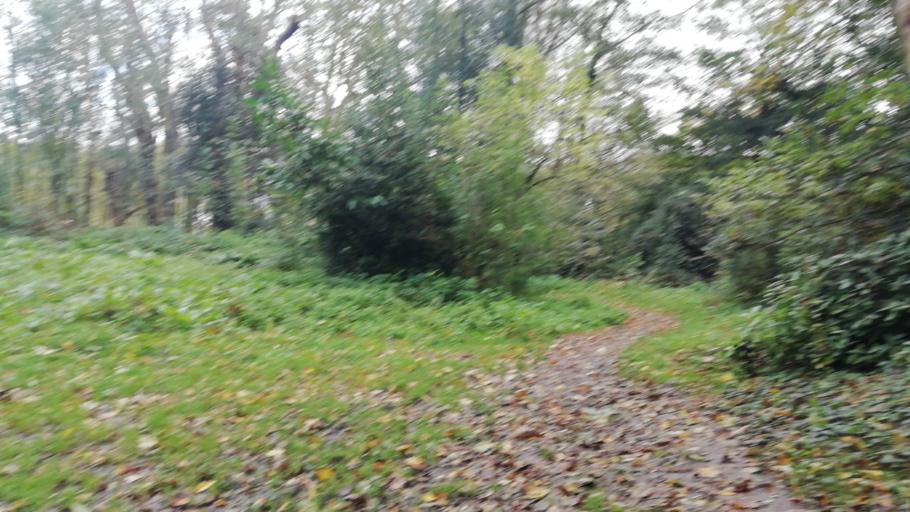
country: FR
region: Haute-Normandie
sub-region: Departement de la Seine-Maritime
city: Sainte-Adresse
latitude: 49.5133
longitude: 0.0819
